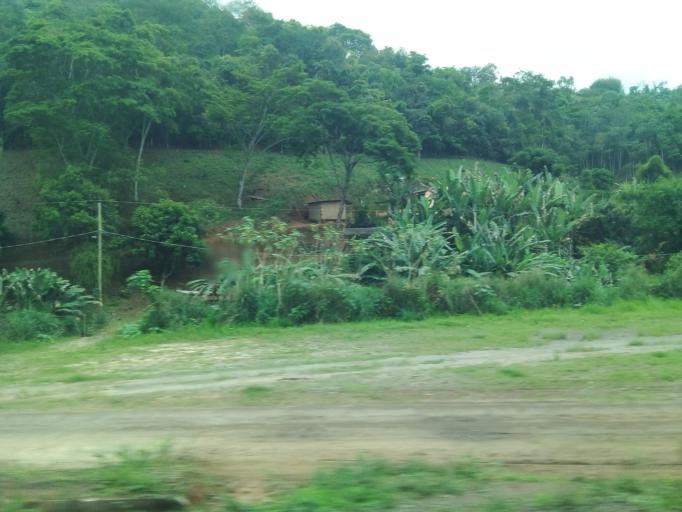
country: BR
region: Minas Gerais
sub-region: Rio Piracicaba
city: Rio Piracicaba
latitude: -19.9620
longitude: -43.2631
